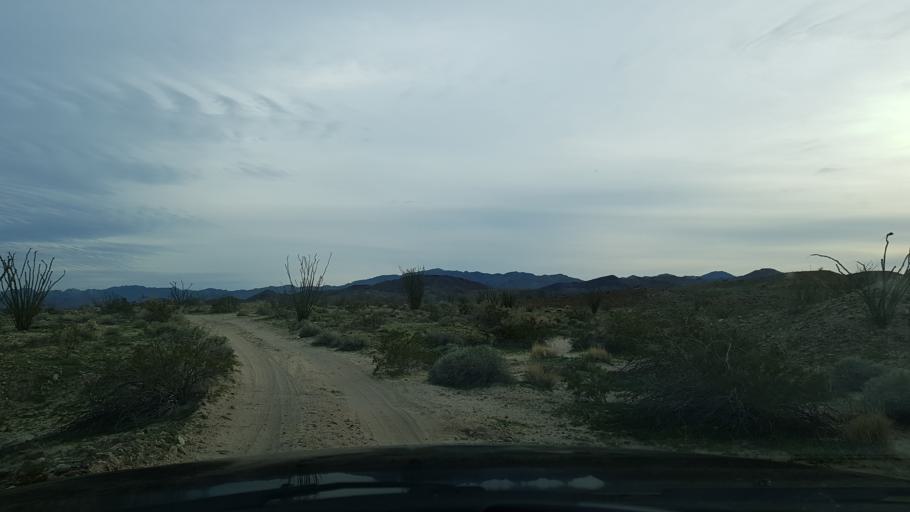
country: MX
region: Baja California
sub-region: Tecate
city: Cereso del Hongo
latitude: 32.8176
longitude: -116.1313
